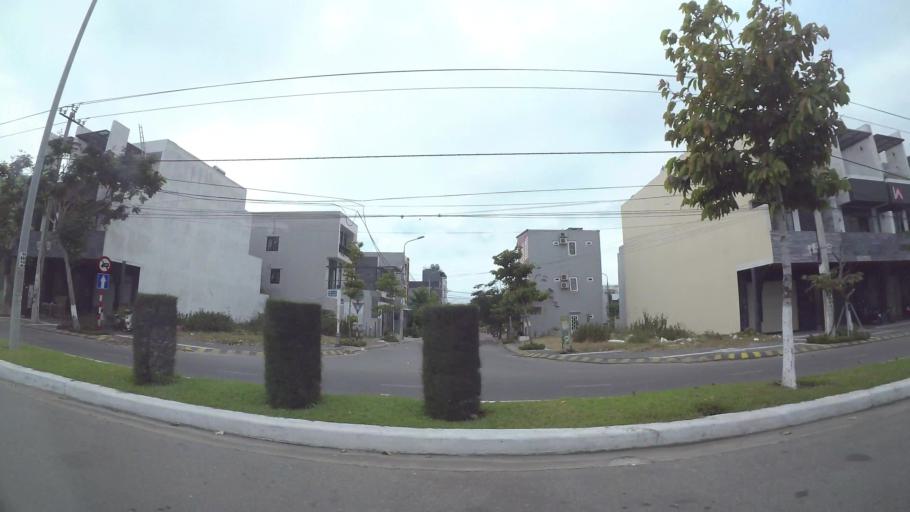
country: VN
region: Da Nang
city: Da Nang
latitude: 16.0999
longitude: 108.2467
